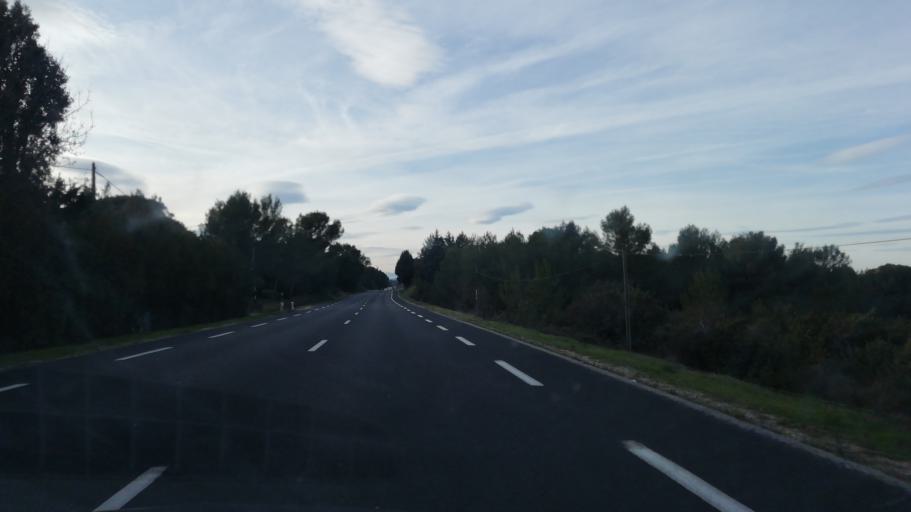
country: FR
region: Languedoc-Roussillon
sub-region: Departement du Gard
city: Caveirac
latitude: 43.8553
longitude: 4.2516
